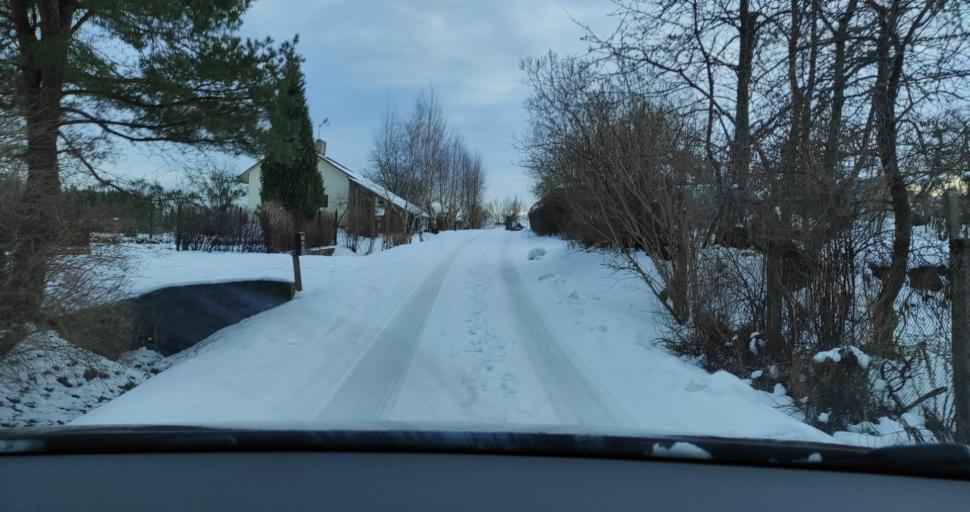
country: LV
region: Kuldigas Rajons
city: Kuldiga
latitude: 56.9436
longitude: 22.0059
